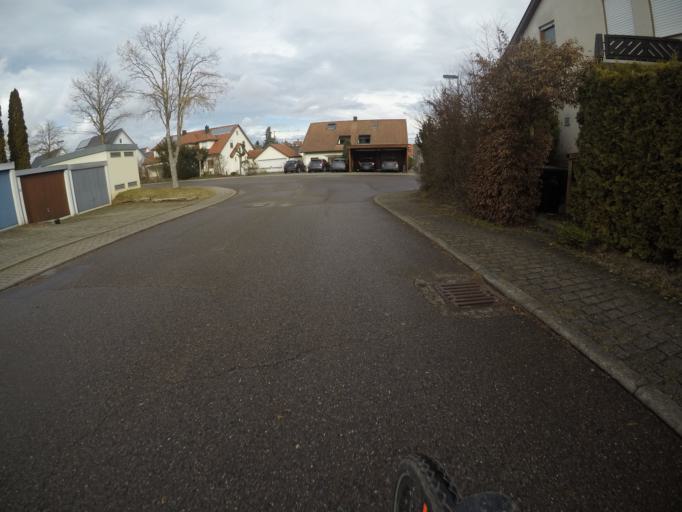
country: DE
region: Baden-Wuerttemberg
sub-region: Regierungsbezirk Stuttgart
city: Herrenberg
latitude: 48.6080
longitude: 8.8443
